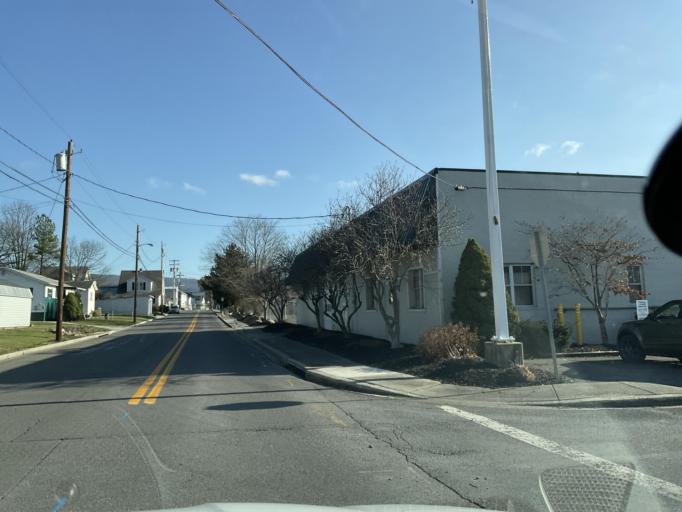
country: US
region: West Virginia
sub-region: Mineral County
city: Wiley Ford
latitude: 39.6293
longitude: -78.7701
